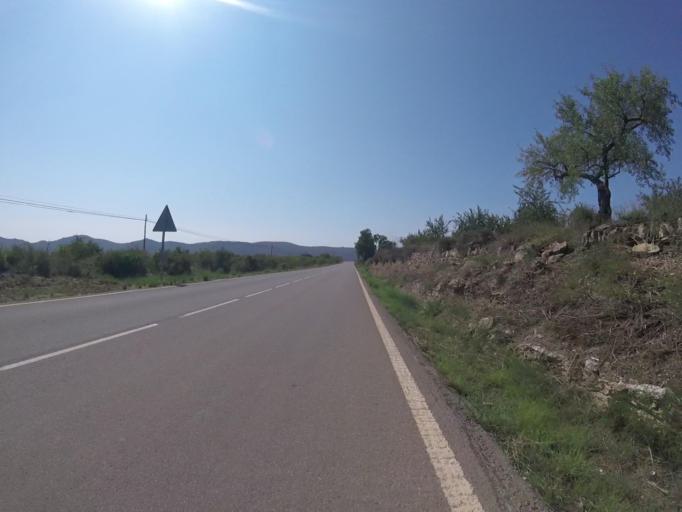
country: ES
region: Valencia
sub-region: Provincia de Castello
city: Adzaneta
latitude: 40.2328
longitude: -0.1771
